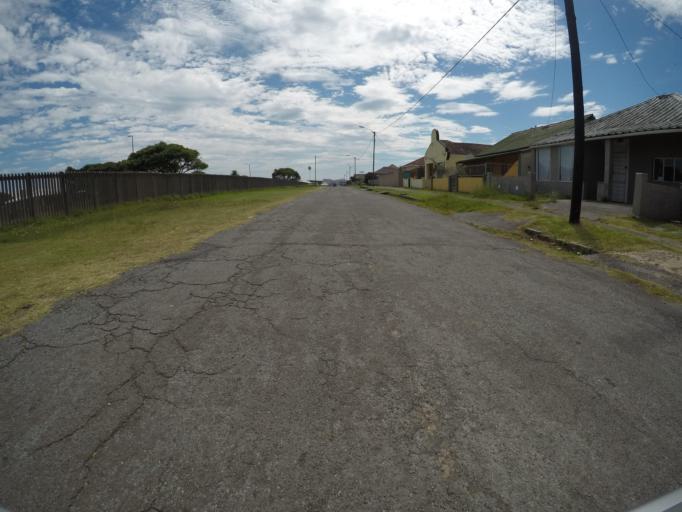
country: ZA
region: Eastern Cape
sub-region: Buffalo City Metropolitan Municipality
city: East London
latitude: -33.0325
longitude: 27.9067
